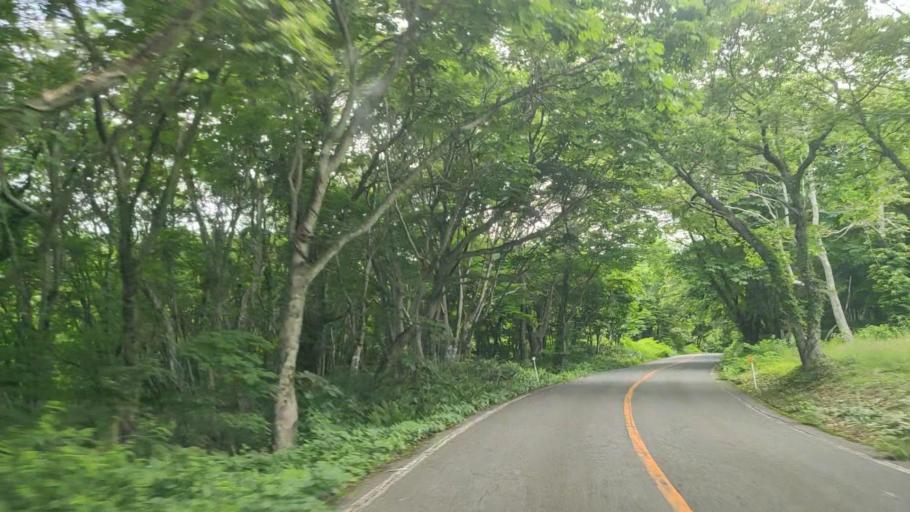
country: JP
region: Tottori
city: Yonago
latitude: 35.3405
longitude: 133.5556
